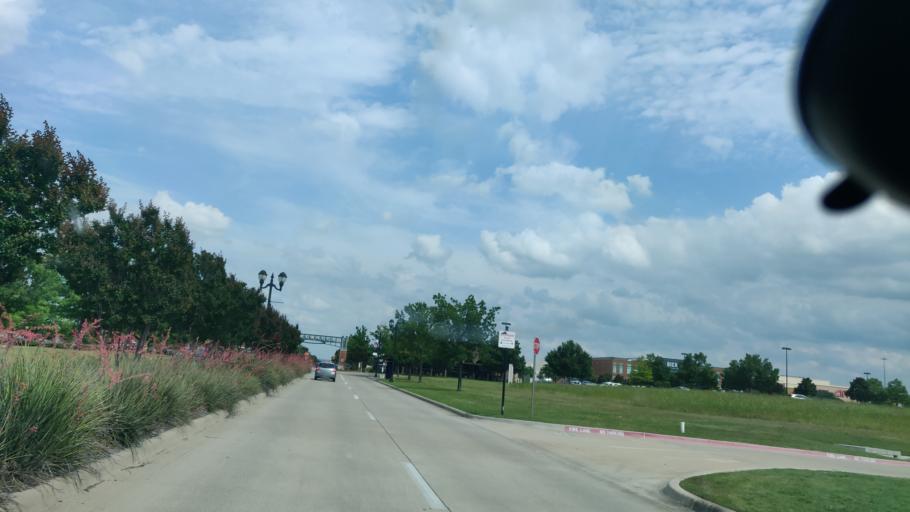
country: US
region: Texas
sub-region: Dallas County
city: Sachse
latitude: 32.9539
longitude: -96.6160
